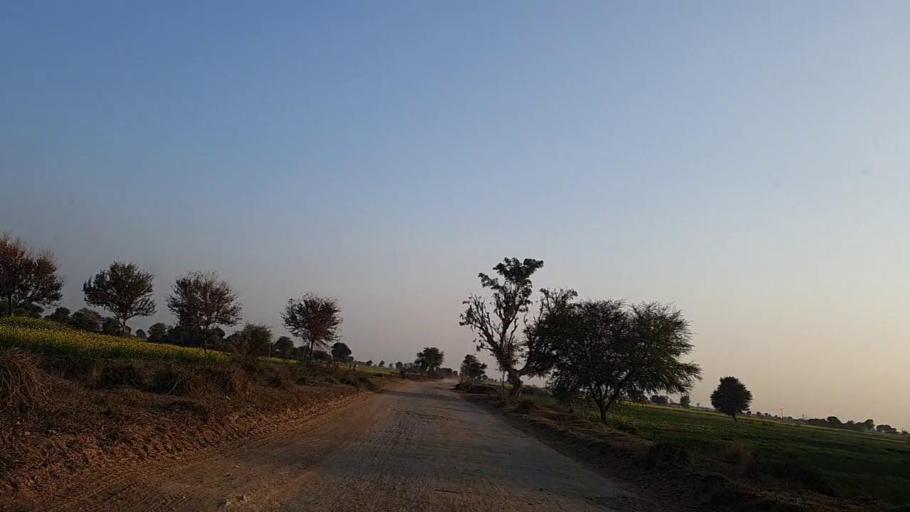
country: PK
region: Sindh
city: Shahdadpur
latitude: 26.0153
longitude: 68.4902
